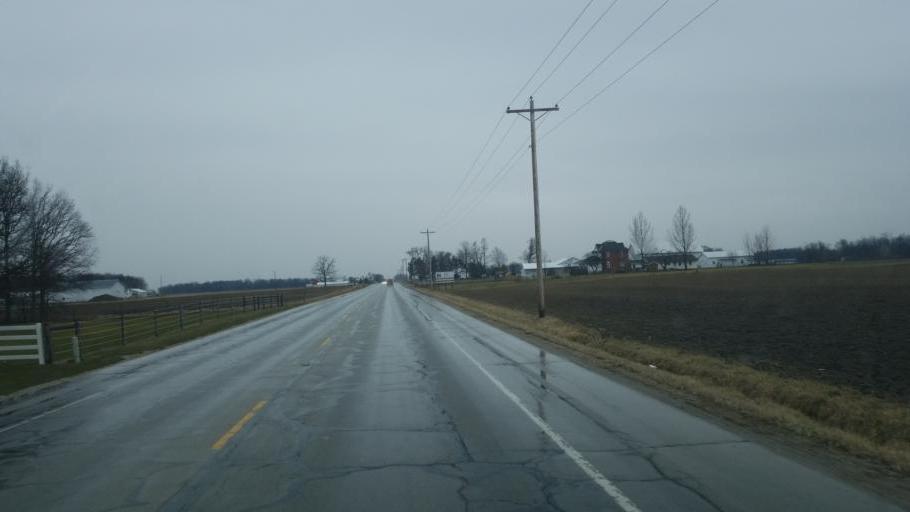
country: US
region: Indiana
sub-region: Adams County
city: Berne
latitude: 40.6973
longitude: -84.9559
